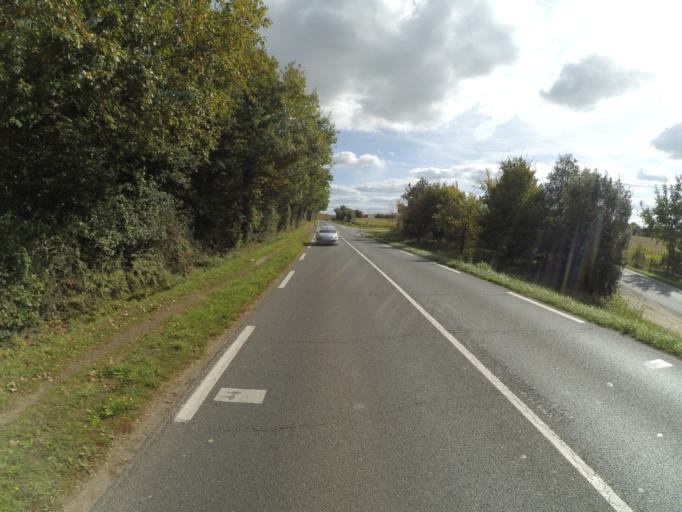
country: FR
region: Pays de la Loire
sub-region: Departement de la Loire-Atlantique
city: Carquefou
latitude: 47.2903
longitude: -1.4676
